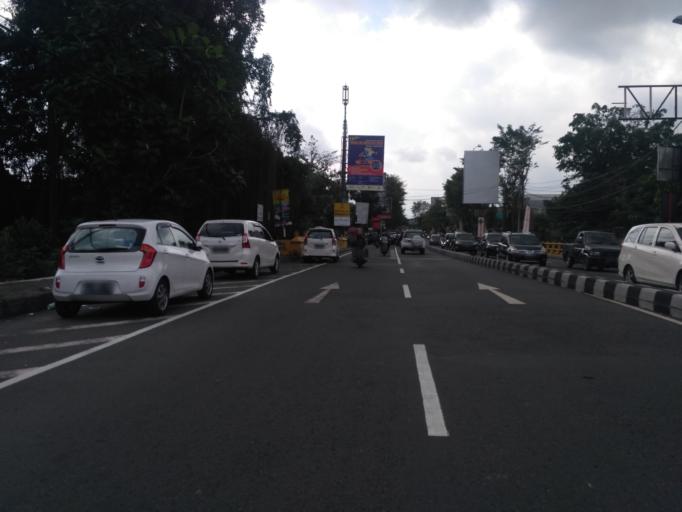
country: ID
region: Daerah Istimewa Yogyakarta
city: Melati
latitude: -7.7451
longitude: 110.3625
